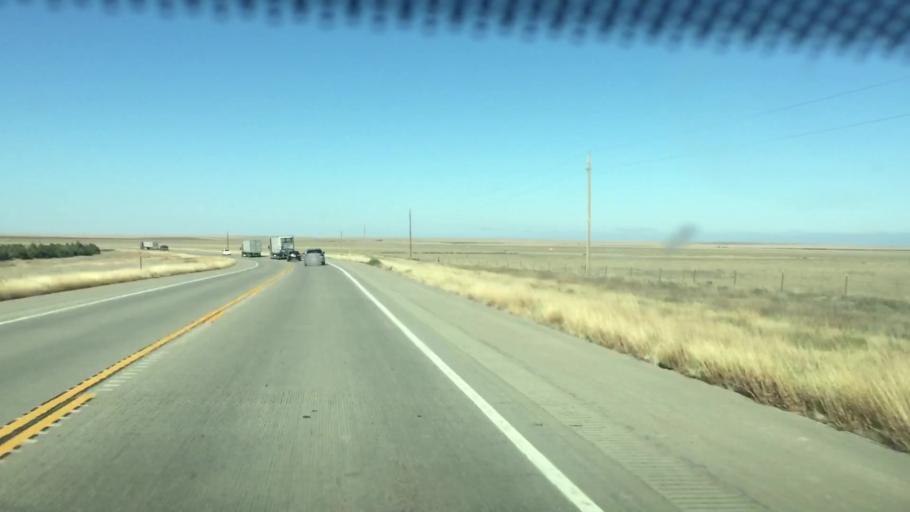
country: US
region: Colorado
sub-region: Prowers County
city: Lamar
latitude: 38.2713
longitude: -102.7215
